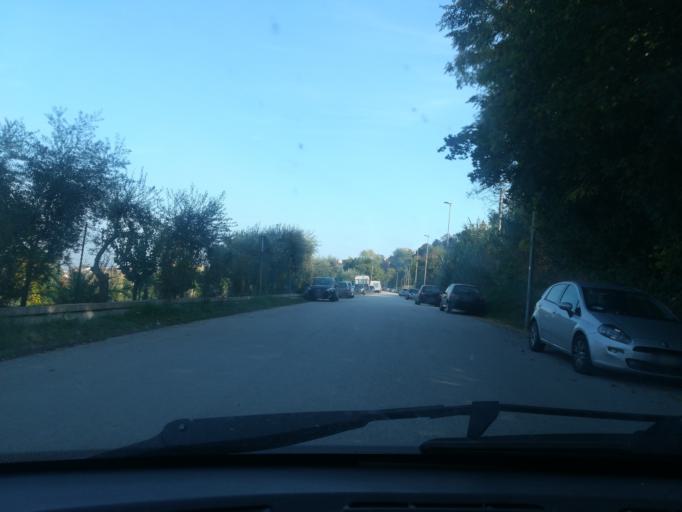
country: IT
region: The Marches
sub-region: Provincia di Macerata
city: Macerata
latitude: 43.3032
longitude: 13.4525
